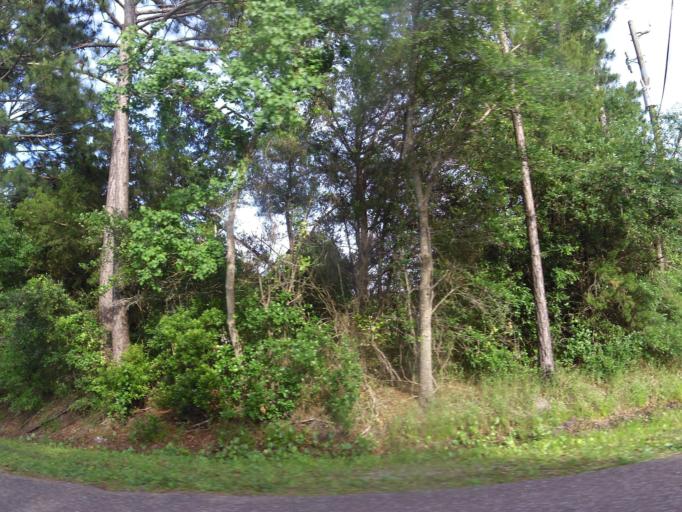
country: US
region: Florida
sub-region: Nassau County
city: Fernandina Beach
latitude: 30.5236
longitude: -81.4937
